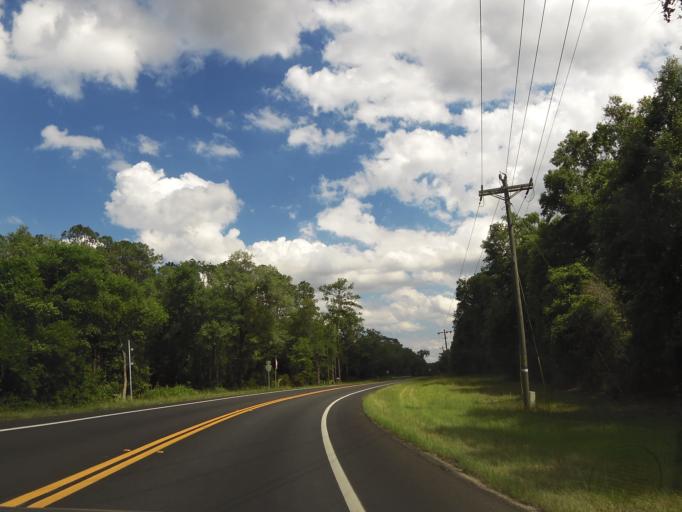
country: US
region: Florida
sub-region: Clay County
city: Keystone Heights
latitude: 29.8083
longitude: -81.9209
